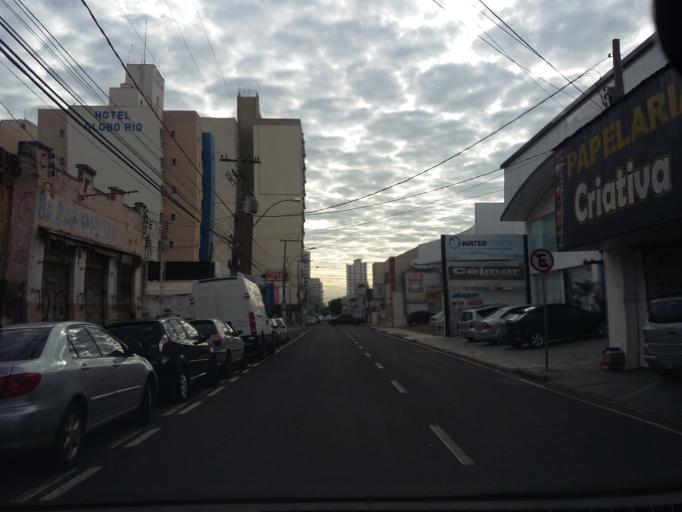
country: BR
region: Sao Paulo
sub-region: Sao Jose Do Rio Preto
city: Sao Jose do Rio Preto
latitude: -20.8205
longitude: -49.3904
